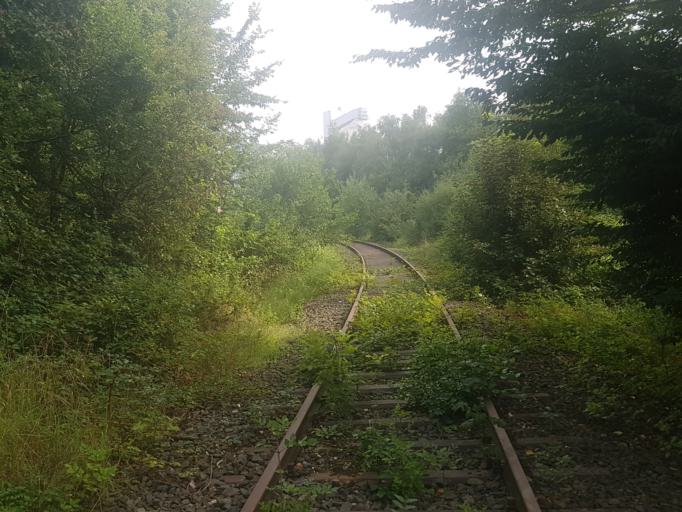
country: DE
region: North Rhine-Westphalia
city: Julich
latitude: 50.9092
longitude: 6.3683
